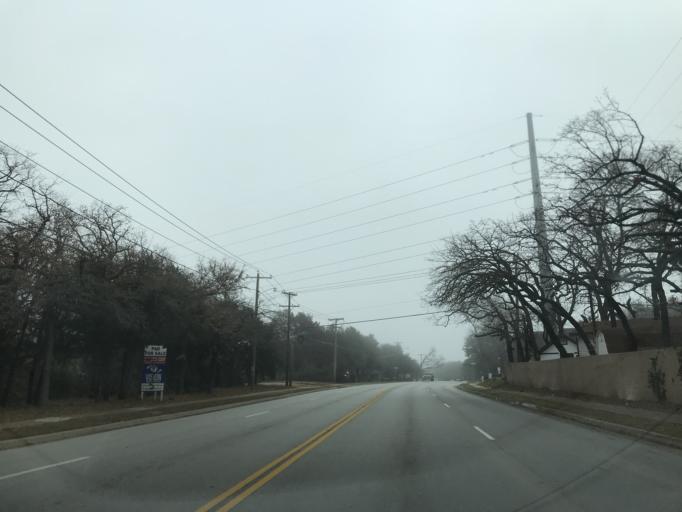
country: US
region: Texas
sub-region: Tarrant County
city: Arlington
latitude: 32.7745
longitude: -97.0699
